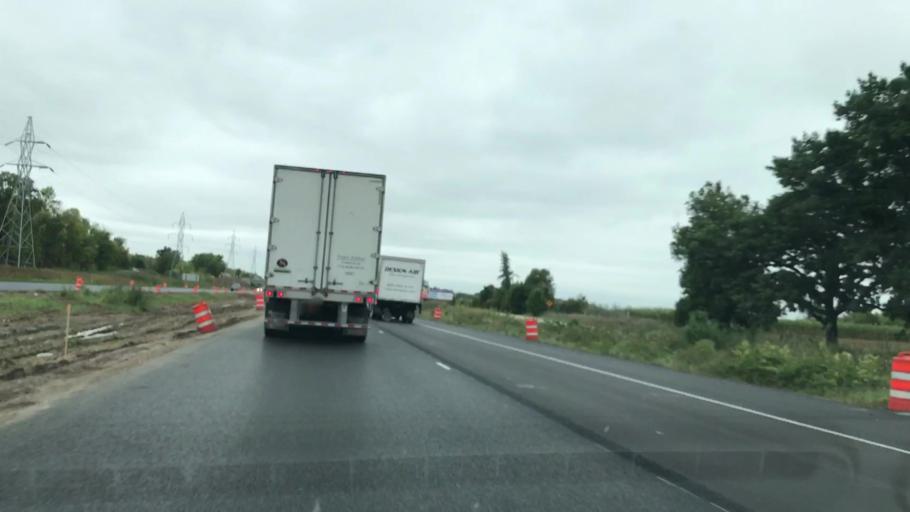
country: US
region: Wisconsin
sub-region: Brown County
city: Suamico
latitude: 44.6258
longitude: -88.0499
